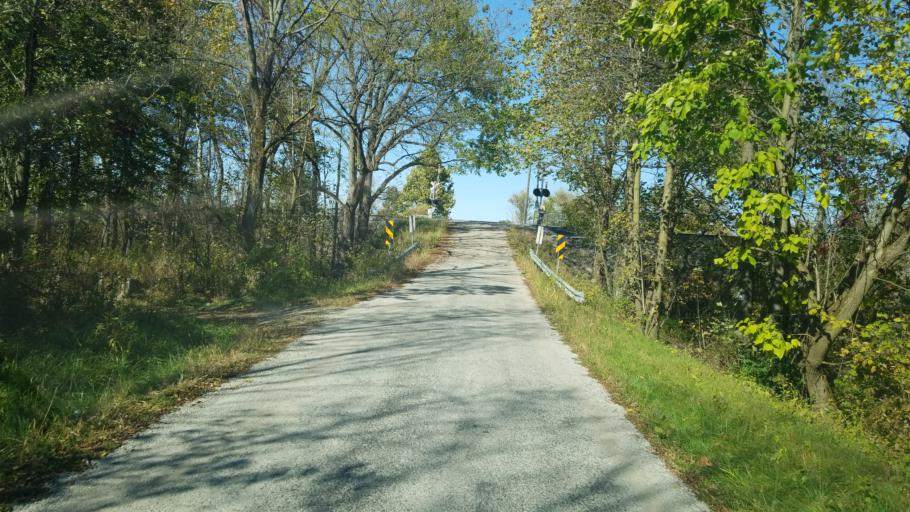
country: US
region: Ohio
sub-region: Huron County
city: New London
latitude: 41.0419
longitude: -82.3458
